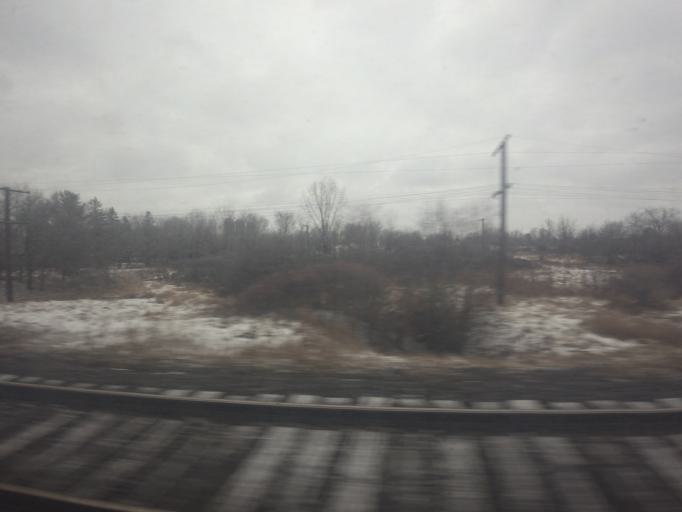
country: CA
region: Ontario
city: Gananoque
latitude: 44.3605
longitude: -76.1814
